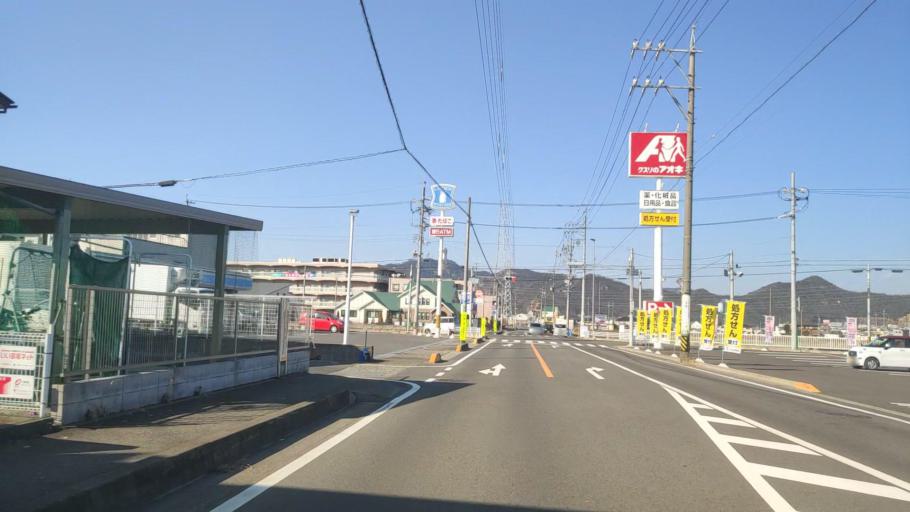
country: JP
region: Gifu
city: Gifu-shi
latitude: 35.4020
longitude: 136.7908
